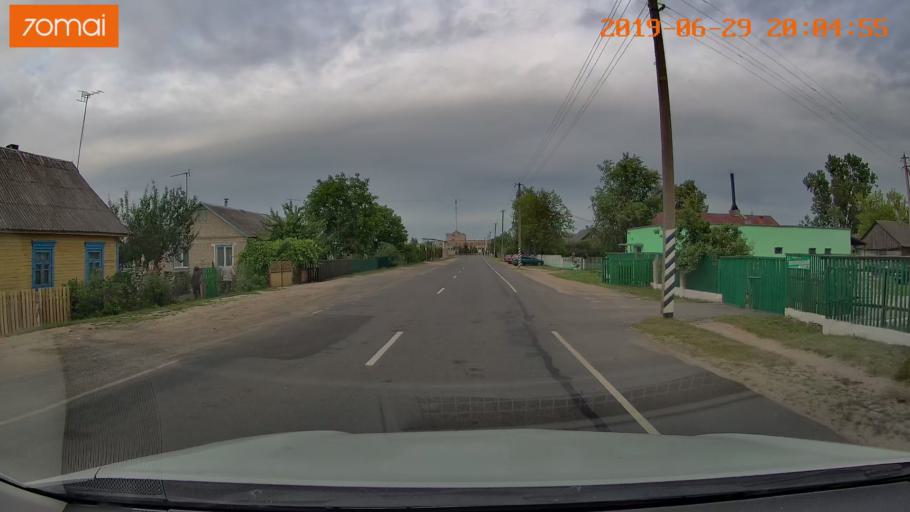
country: BY
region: Brest
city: Lahishyn
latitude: 52.3361
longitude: 25.9970
